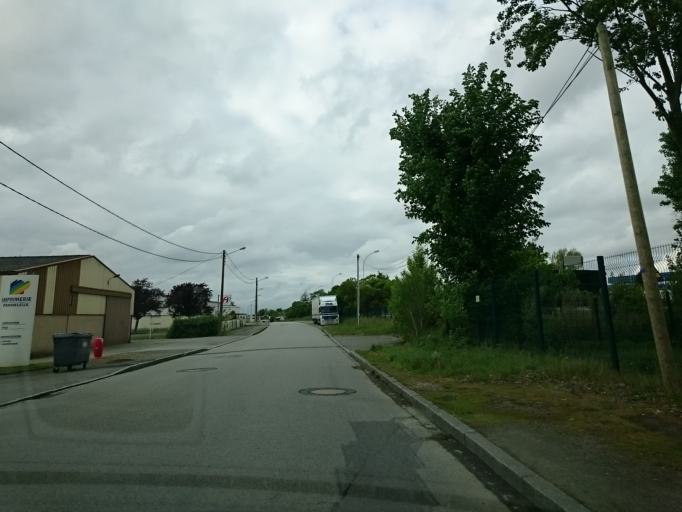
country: FR
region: Brittany
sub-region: Departement d'Ille-et-Vilaine
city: Vern-sur-Seiche
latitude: 48.0520
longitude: -1.6081
